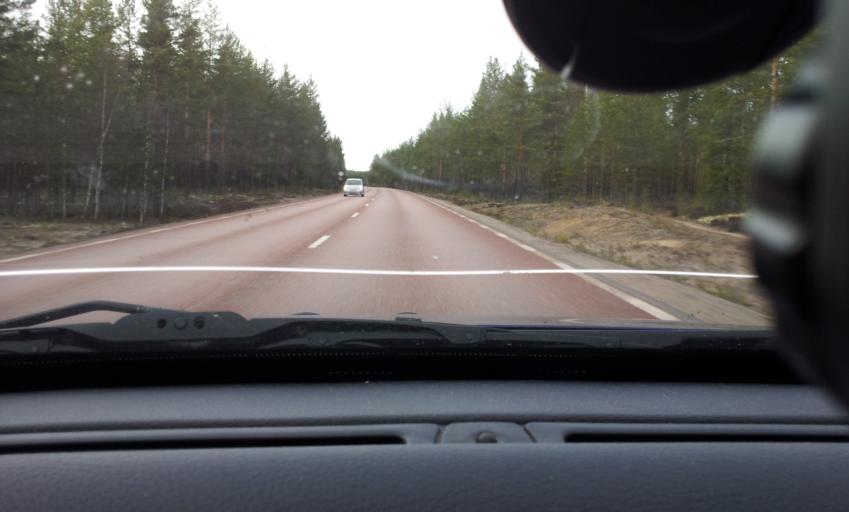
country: SE
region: Gaevleborg
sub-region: Ljusdals Kommun
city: Farila
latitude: 61.8235
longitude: 15.7560
